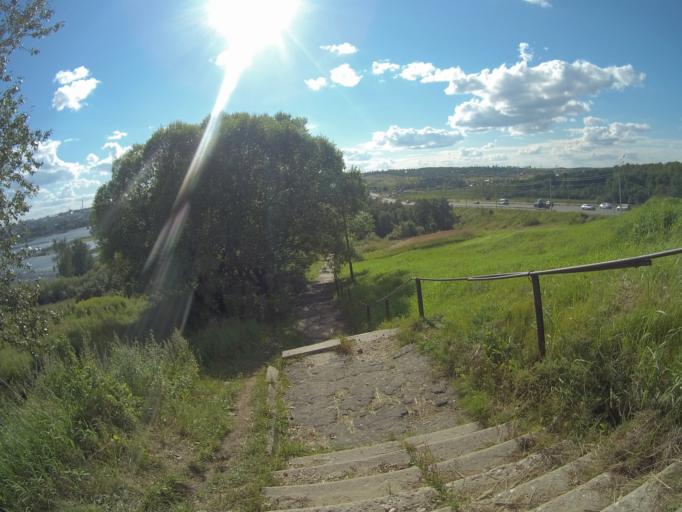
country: RU
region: Vladimir
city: Vladimir
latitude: 56.1720
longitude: 40.4324
